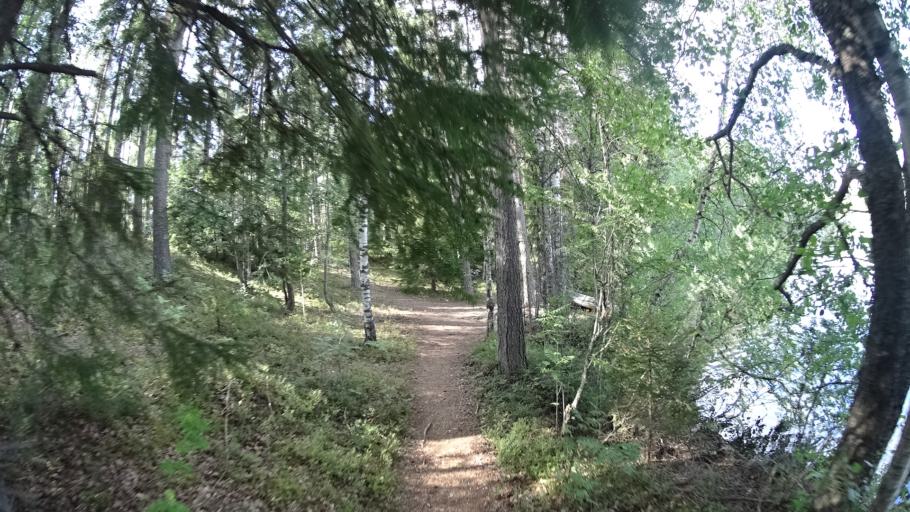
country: FI
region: Uusimaa
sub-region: Helsinki
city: Kaerkoelae
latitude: 60.7374
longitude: 24.0550
